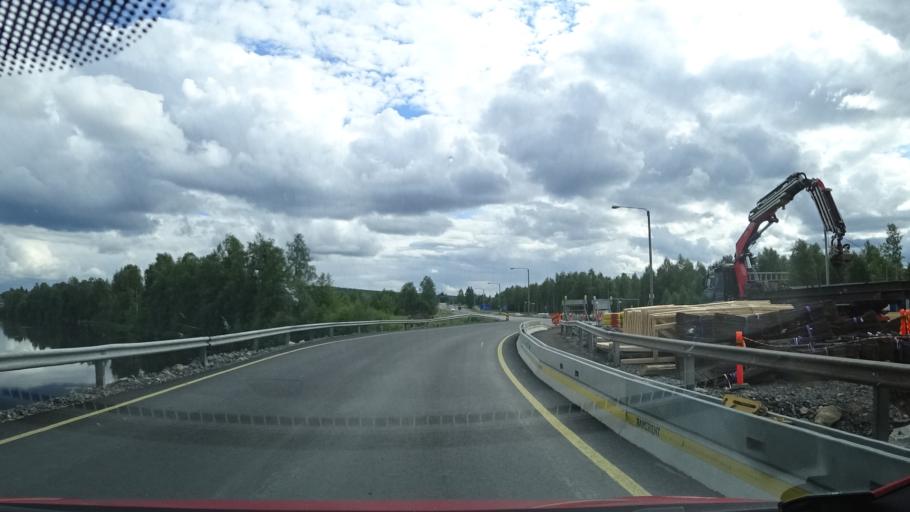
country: FI
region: Lapland
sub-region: Rovaniemi
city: Rovaniemi
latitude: 66.5234
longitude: 25.7456
